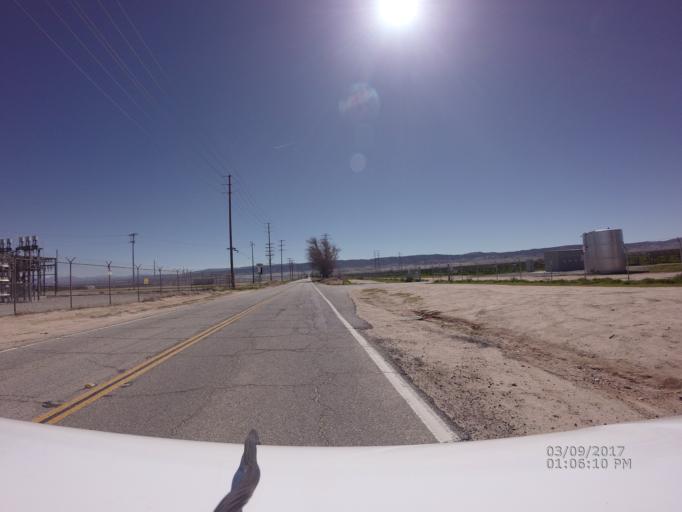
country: US
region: California
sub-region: Los Angeles County
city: Leona Valley
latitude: 34.7181
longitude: -118.2896
